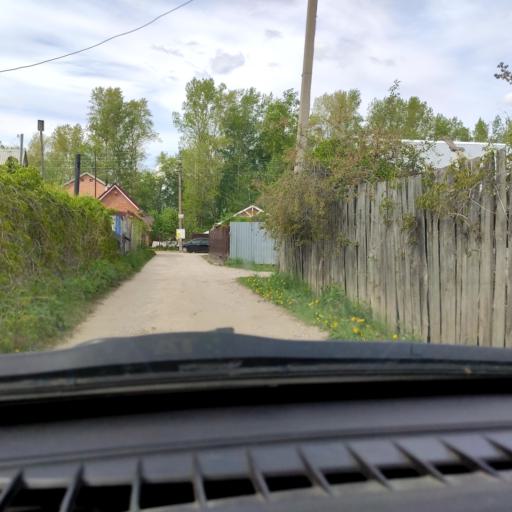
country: RU
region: Samara
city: Zhigulevsk
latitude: 53.4587
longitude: 49.5184
